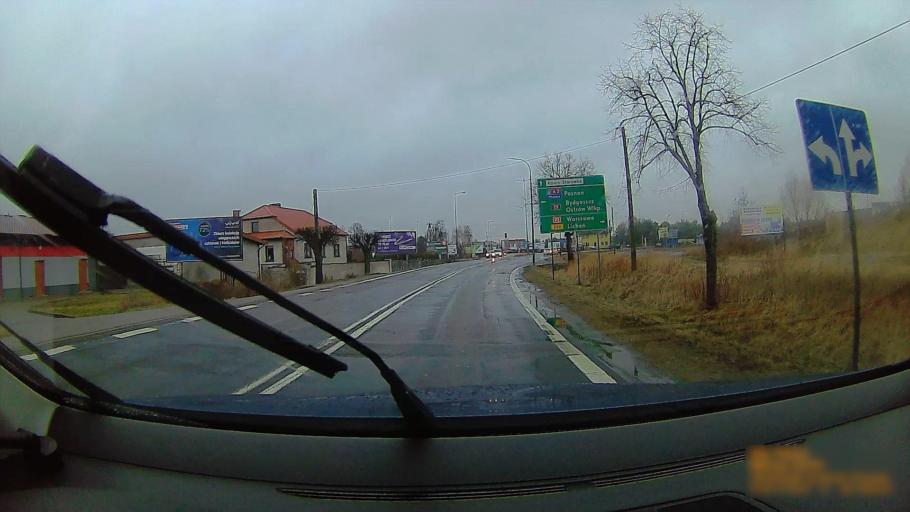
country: PL
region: Greater Poland Voivodeship
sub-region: Konin
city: Konin
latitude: 52.1906
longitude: 18.2645
